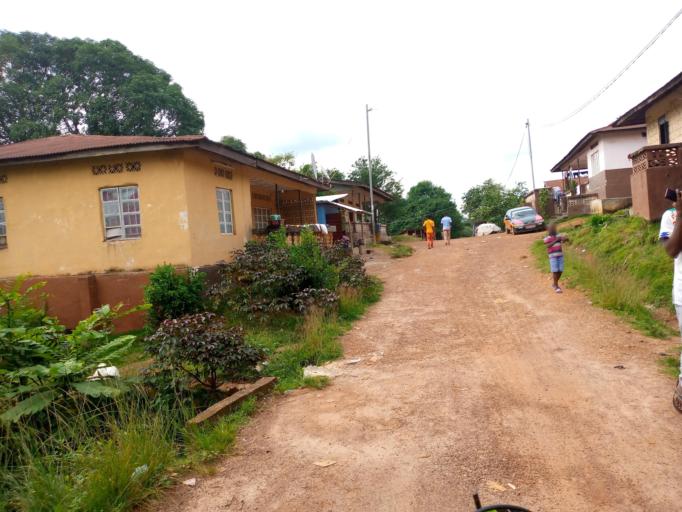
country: SL
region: Northern Province
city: Magburaka
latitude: 8.7235
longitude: -11.9429
